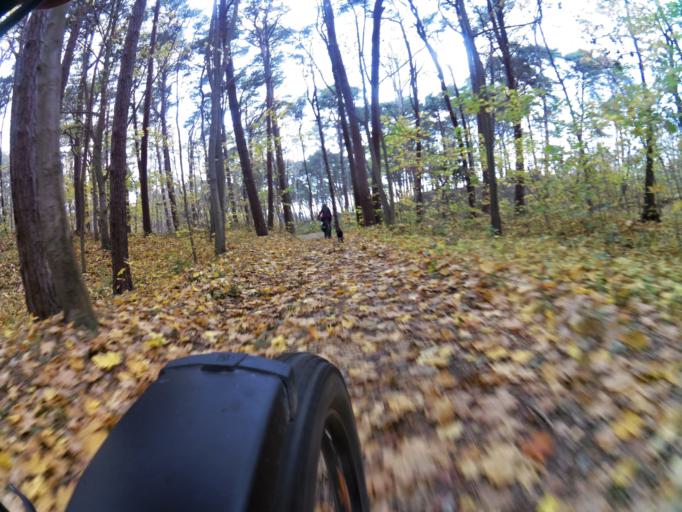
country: PL
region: Pomeranian Voivodeship
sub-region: Powiat pucki
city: Jastarnia
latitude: 54.7175
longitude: 18.6339
